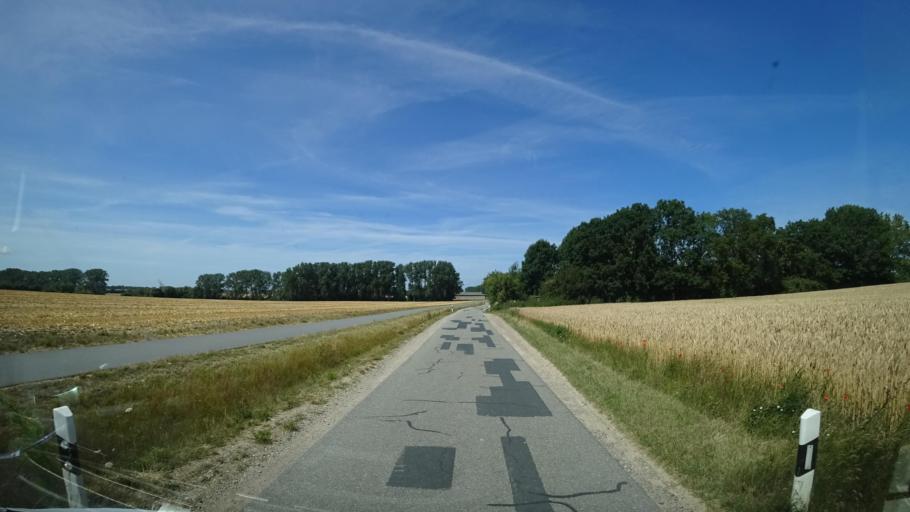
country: DE
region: Mecklenburg-Vorpommern
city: Blowatz
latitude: 54.0209
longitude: 11.5577
